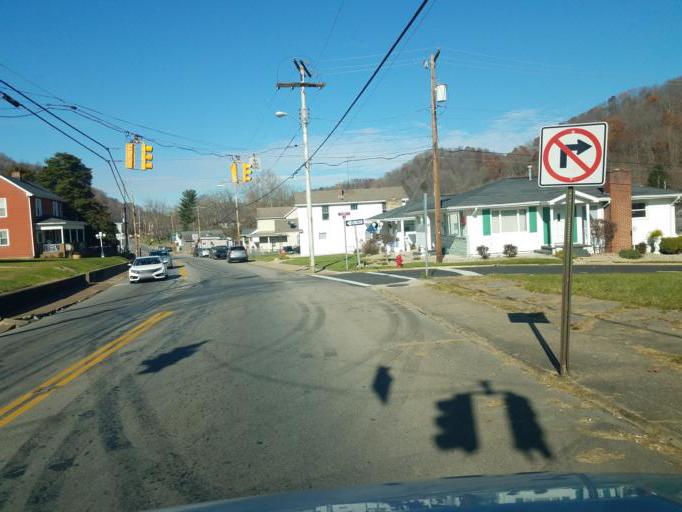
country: US
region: Ohio
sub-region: Scioto County
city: New Boston
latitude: 38.7604
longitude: -82.9334
